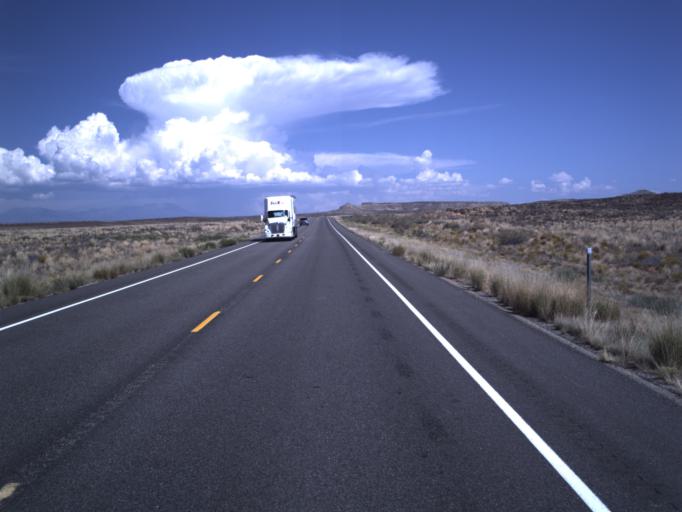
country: US
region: Utah
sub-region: San Juan County
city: Blanding
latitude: 37.3130
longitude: -109.5261
